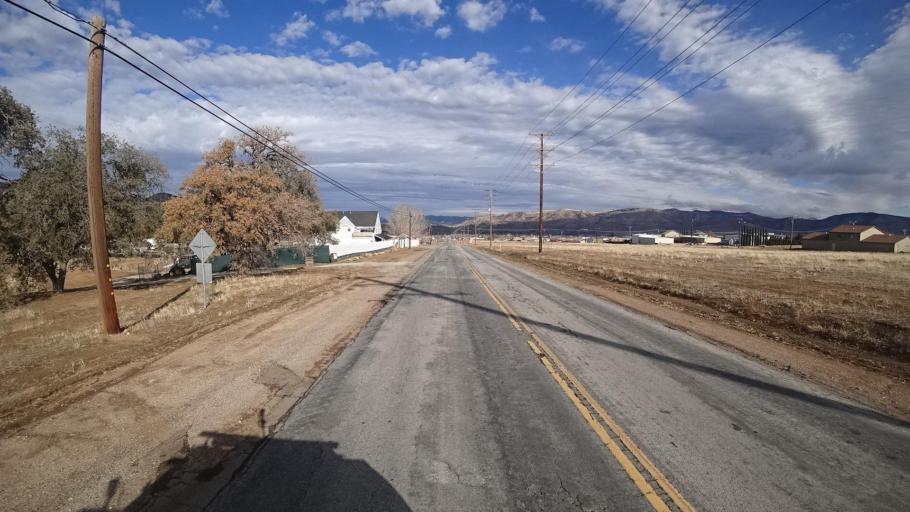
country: US
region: California
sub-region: Kern County
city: Golden Hills
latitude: 35.1180
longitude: -118.4948
